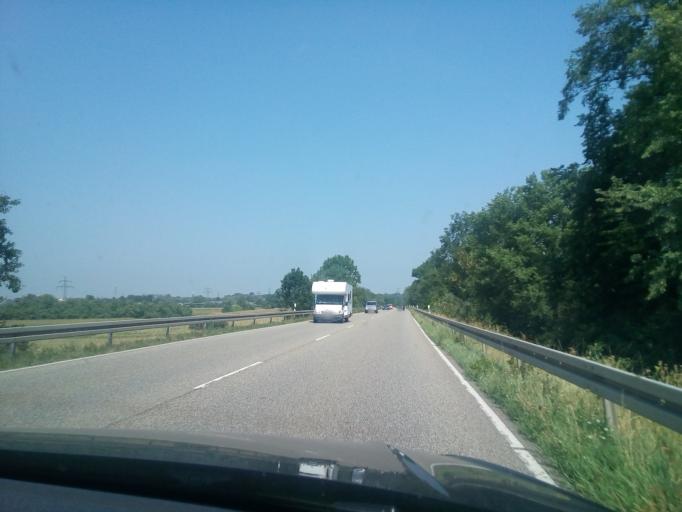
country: DE
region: Baden-Wuerttemberg
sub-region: Freiburg Region
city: Achern
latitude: 48.6306
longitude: 8.0517
